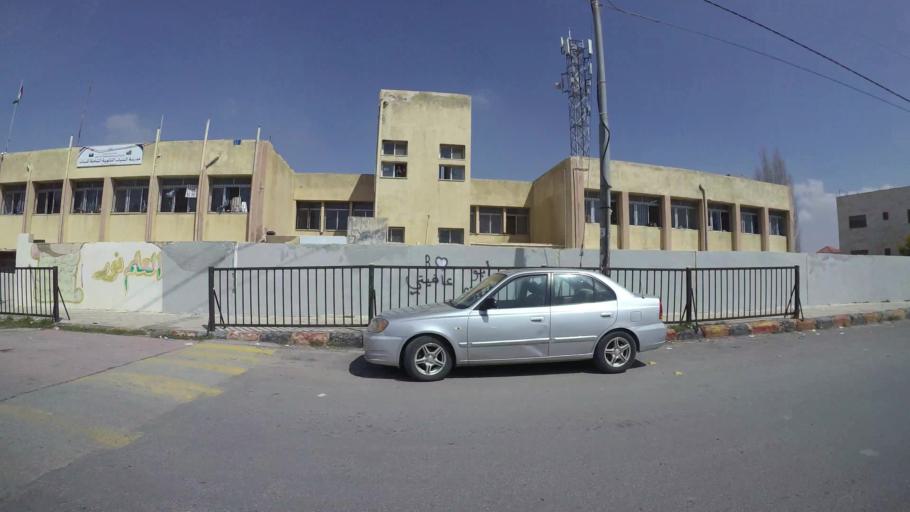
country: JO
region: Amman
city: Al Bunayyat ash Shamaliyah
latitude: 31.8969
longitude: 35.8885
